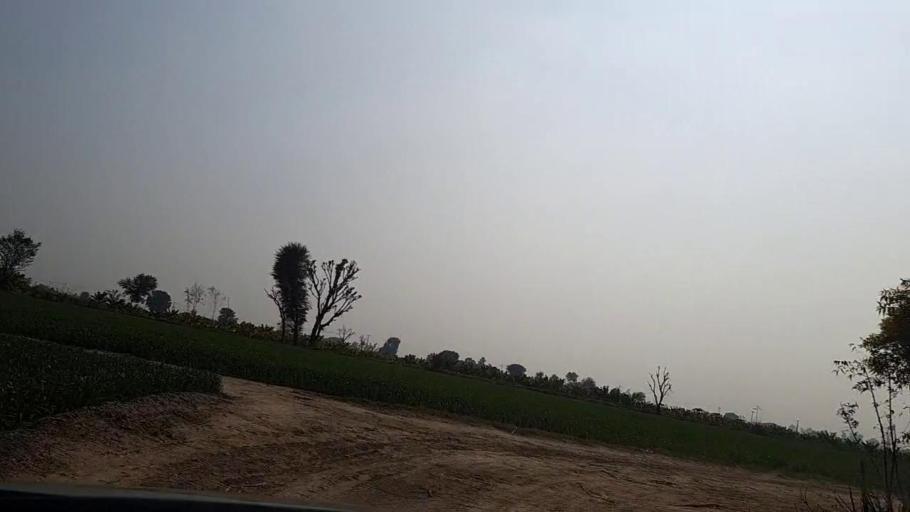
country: PK
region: Sindh
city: Sakrand
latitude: 26.1423
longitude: 68.2348
